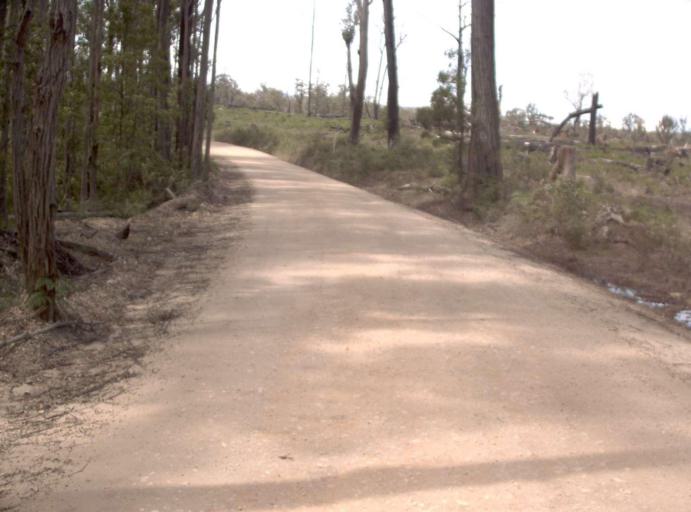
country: AU
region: Victoria
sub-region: East Gippsland
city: Lakes Entrance
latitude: -37.6271
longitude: 148.6778
